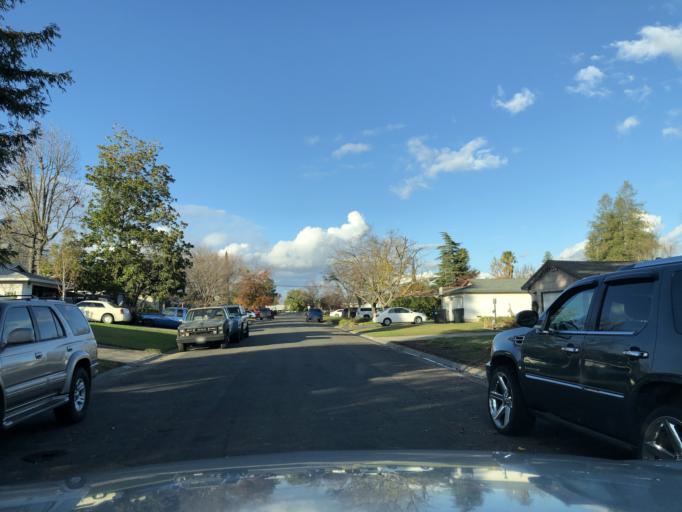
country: US
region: California
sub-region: Sacramento County
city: Fair Oaks
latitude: 38.6619
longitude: -121.3116
